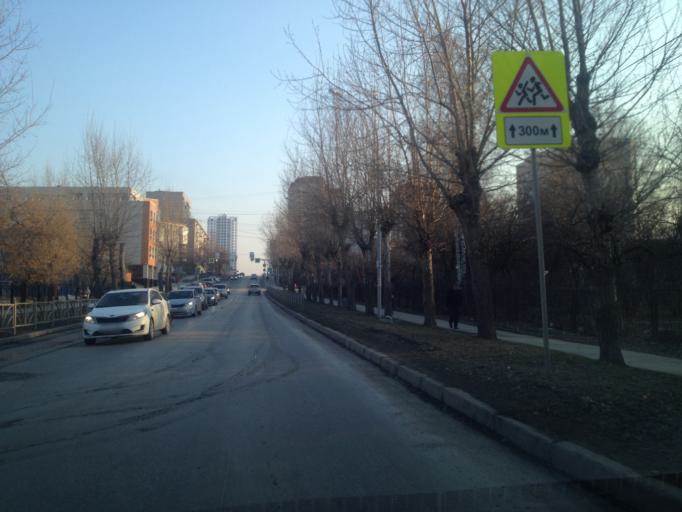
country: RU
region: Sverdlovsk
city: Yekaterinburg
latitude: 56.8295
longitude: 60.5514
